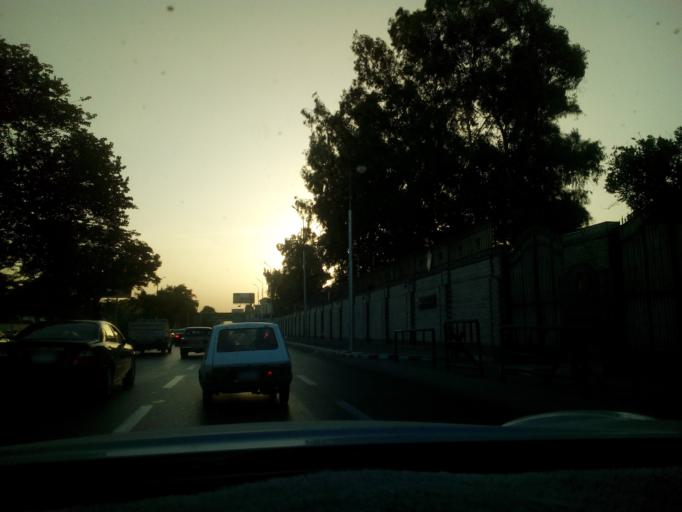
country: EG
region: Muhafazat al Qalyubiyah
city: Al Khankah
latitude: 30.1015
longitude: 31.3529
